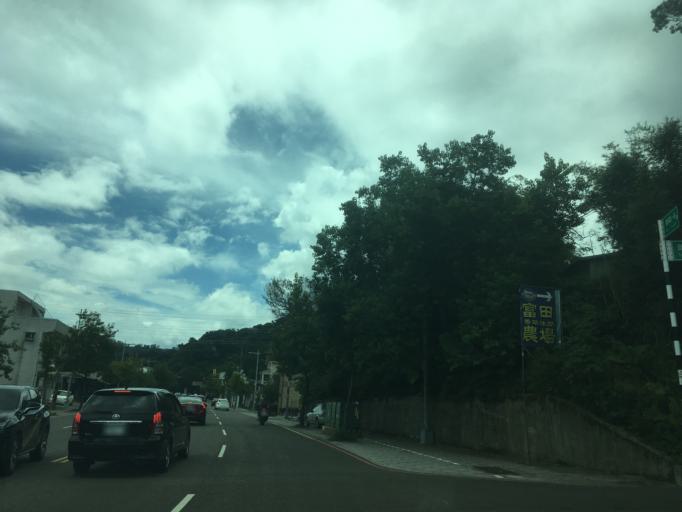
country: TW
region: Taiwan
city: Daxi
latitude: 24.8416
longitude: 121.2884
